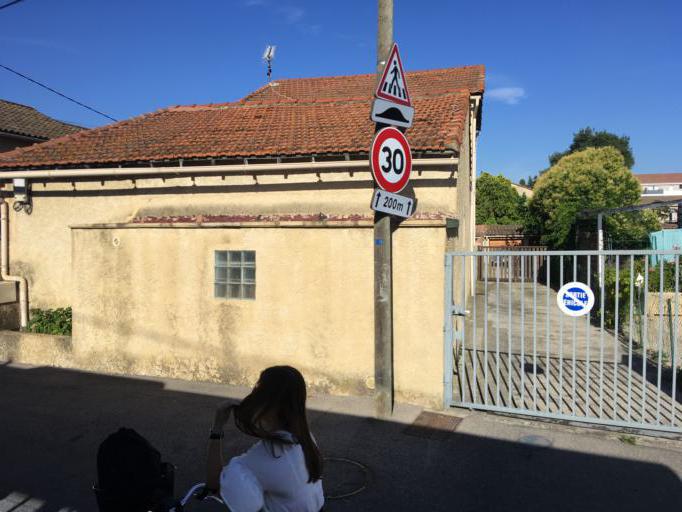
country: FR
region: Provence-Alpes-Cote d'Azur
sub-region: Departement du Vaucluse
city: Avignon
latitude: 43.9498
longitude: 4.8296
